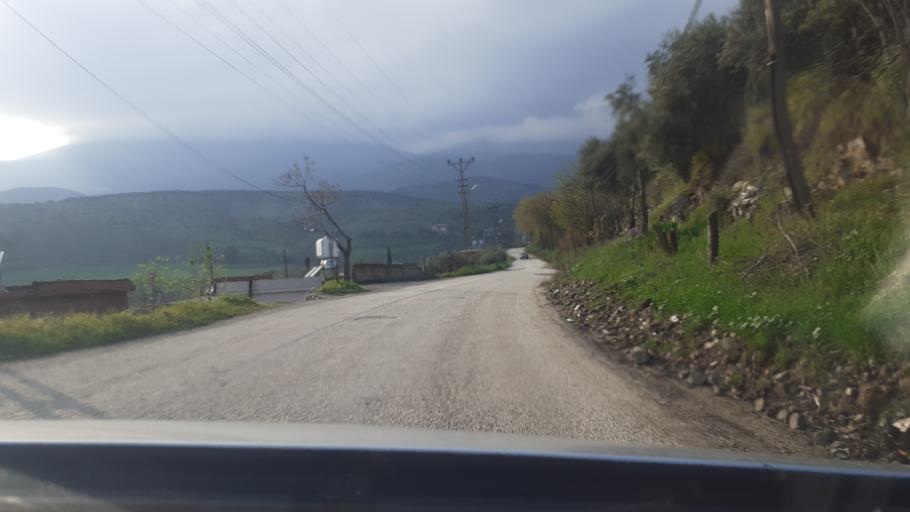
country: TR
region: Hatay
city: Kirikhan
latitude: 36.5013
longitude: 36.3274
